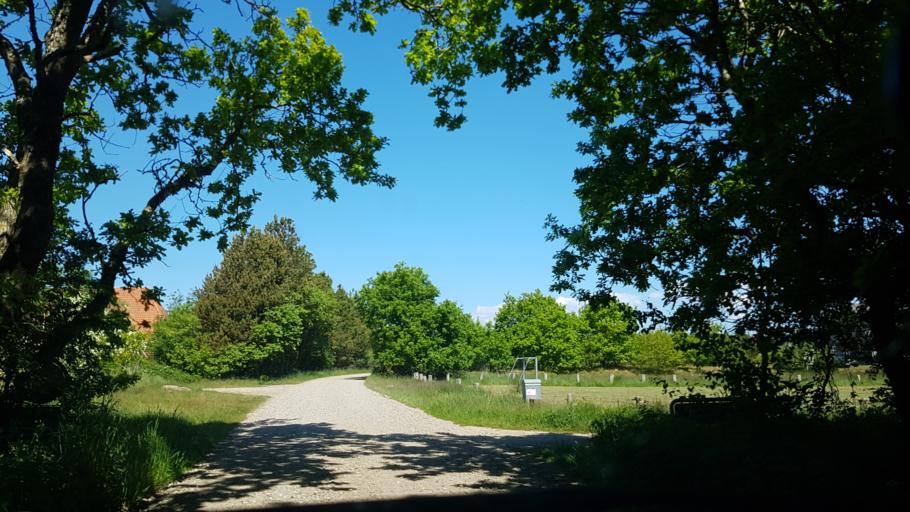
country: DE
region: Schleswig-Holstein
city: List
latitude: 55.1113
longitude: 8.5500
